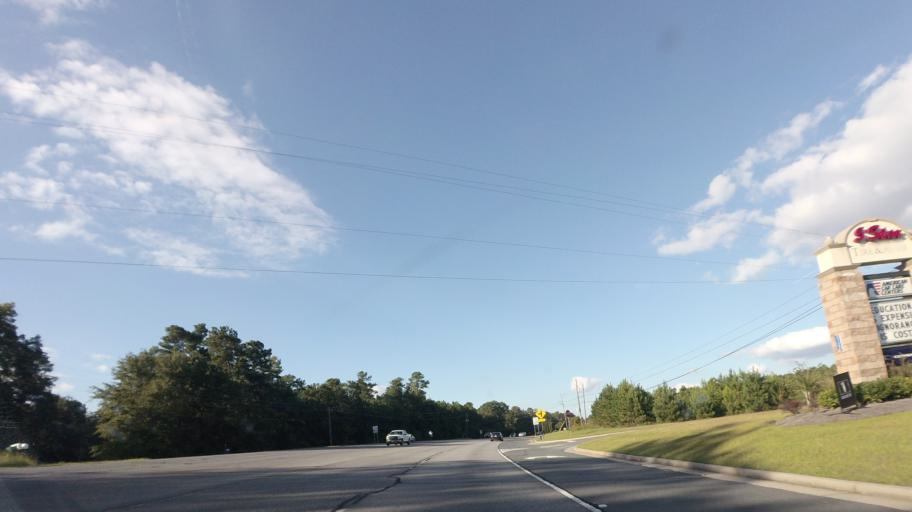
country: US
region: Georgia
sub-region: Upson County
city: Hannahs Mill
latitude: 32.9522
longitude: -84.3381
